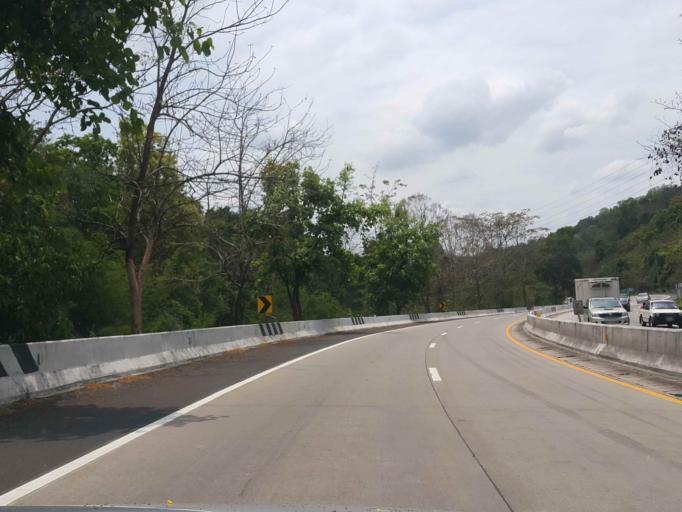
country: TH
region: Lamphun
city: Mae Tha
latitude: 18.4008
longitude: 99.2142
